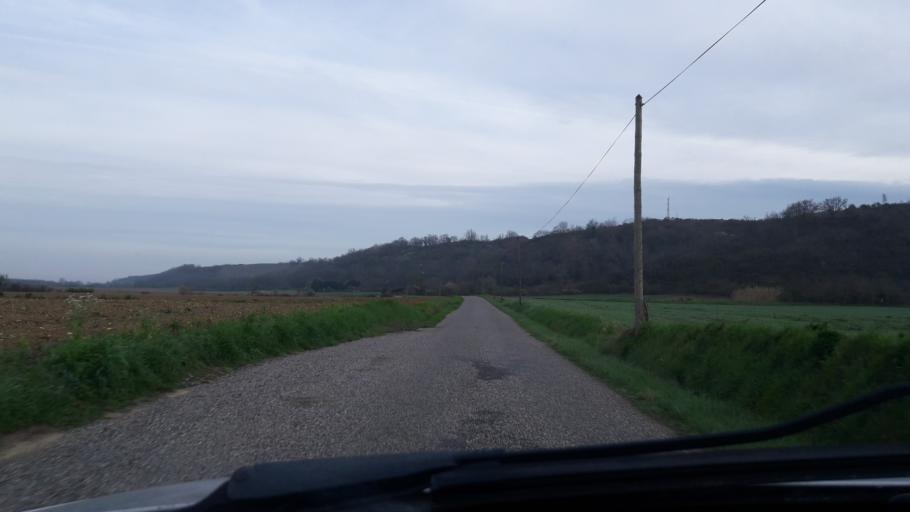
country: FR
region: Midi-Pyrenees
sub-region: Departement de la Haute-Garonne
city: Montesquieu-Volvestre
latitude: 43.1747
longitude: 1.2688
